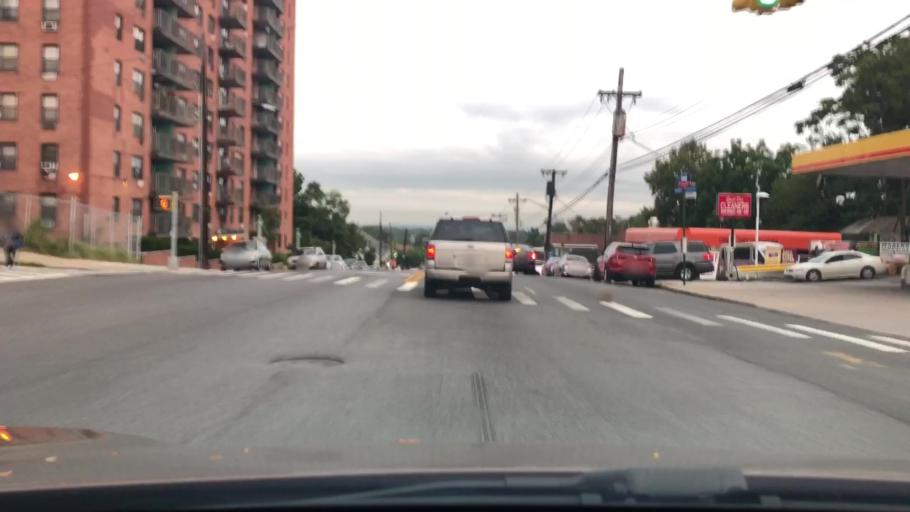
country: US
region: New York
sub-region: Bronx
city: Eastchester
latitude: 40.8921
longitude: -73.8535
